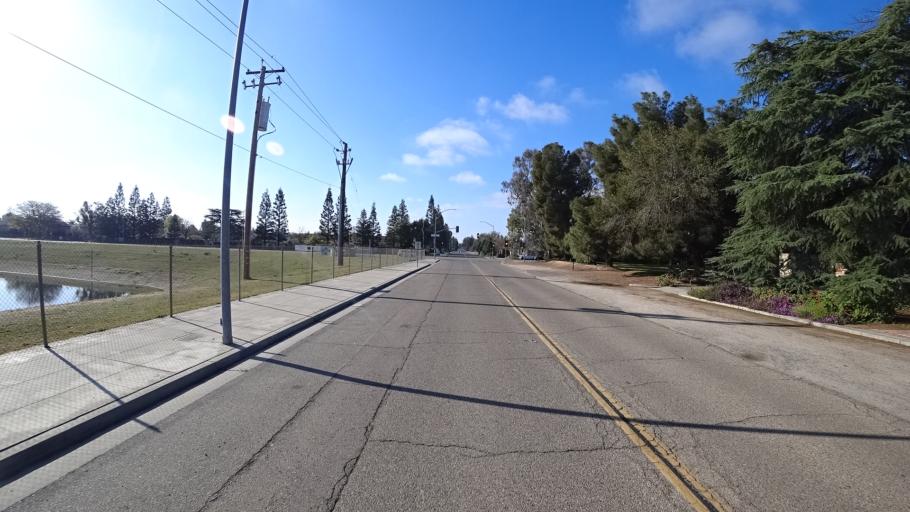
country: US
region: California
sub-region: Fresno County
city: Fresno
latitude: 36.8235
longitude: -119.8308
